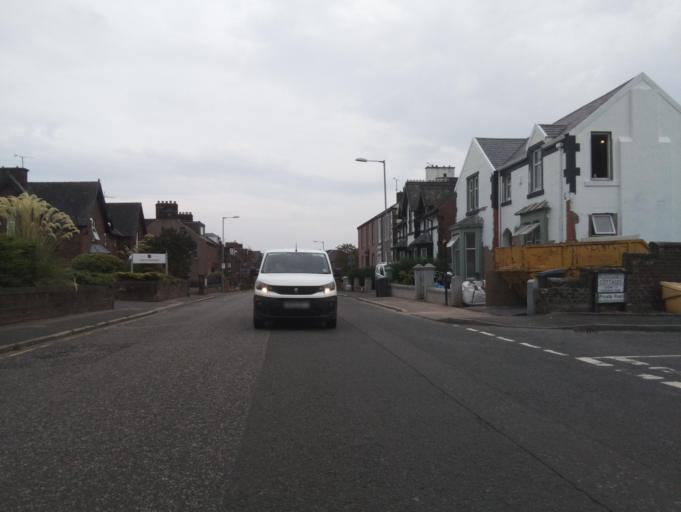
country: GB
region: Scotland
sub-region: Dumfries and Galloway
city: Dumfries
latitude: 55.0704
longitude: -3.5973
